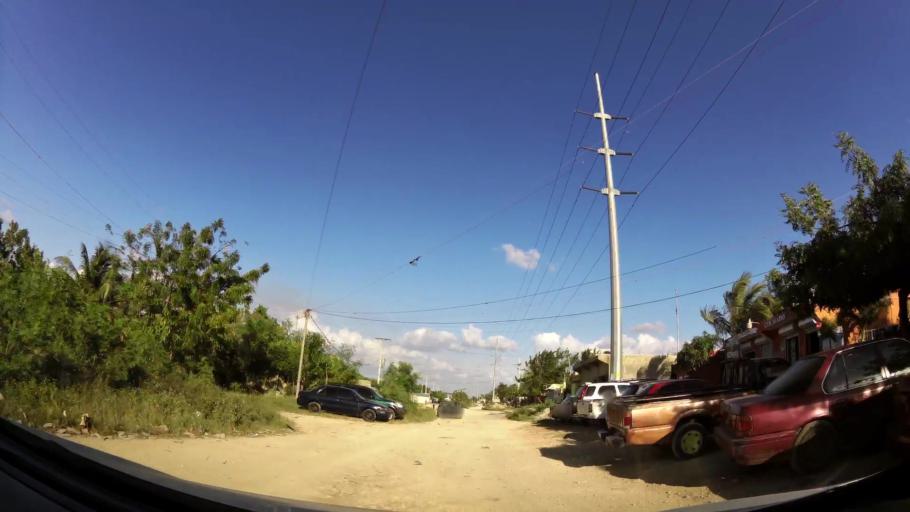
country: DO
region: Santo Domingo
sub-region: Santo Domingo
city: Santo Domingo Este
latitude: 18.4757
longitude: -69.8092
